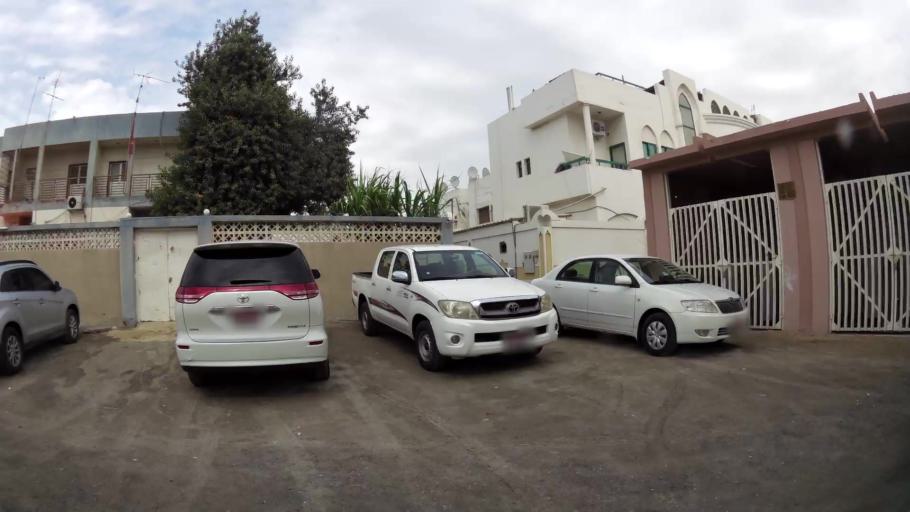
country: AE
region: Abu Dhabi
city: Abu Dhabi
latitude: 24.4286
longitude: 54.4038
